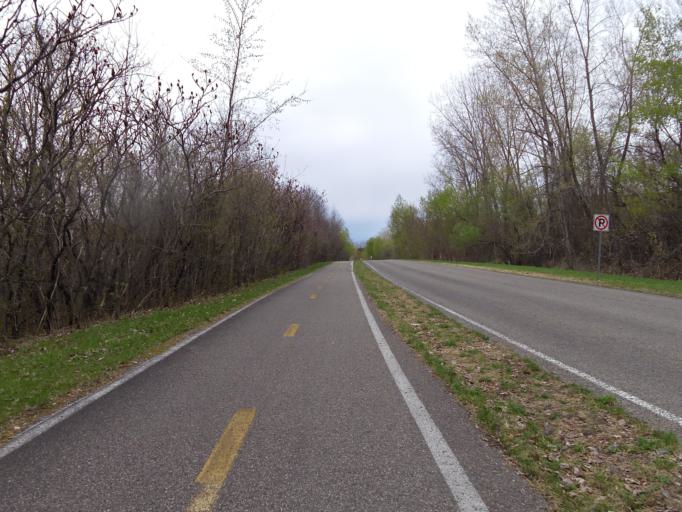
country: CA
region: Quebec
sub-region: Laurentides
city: Oka
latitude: 45.4786
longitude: -74.0473
